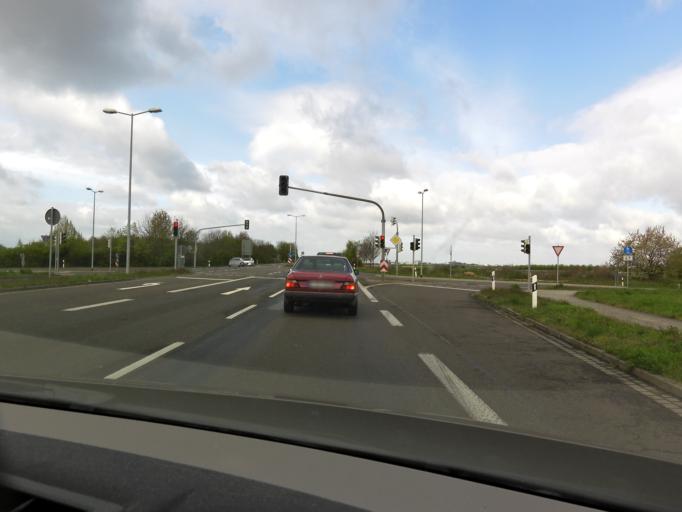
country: DE
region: Saxony
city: Schkeuditz
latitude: 51.4030
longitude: 12.2055
